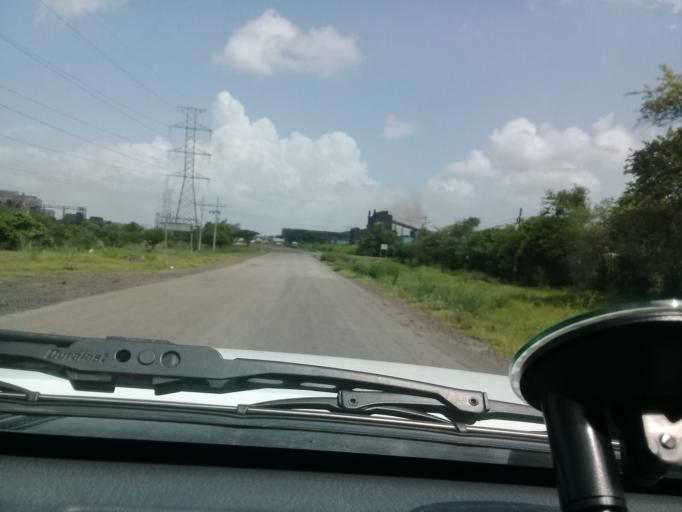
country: MX
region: Veracruz
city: Moralillo
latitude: 22.2306
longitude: -98.0182
